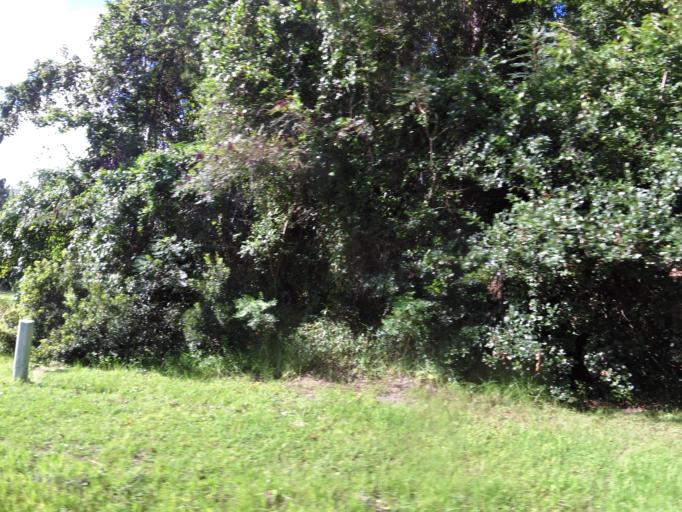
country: US
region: Georgia
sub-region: Camden County
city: Woodbine
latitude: 30.9637
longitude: -81.7242
